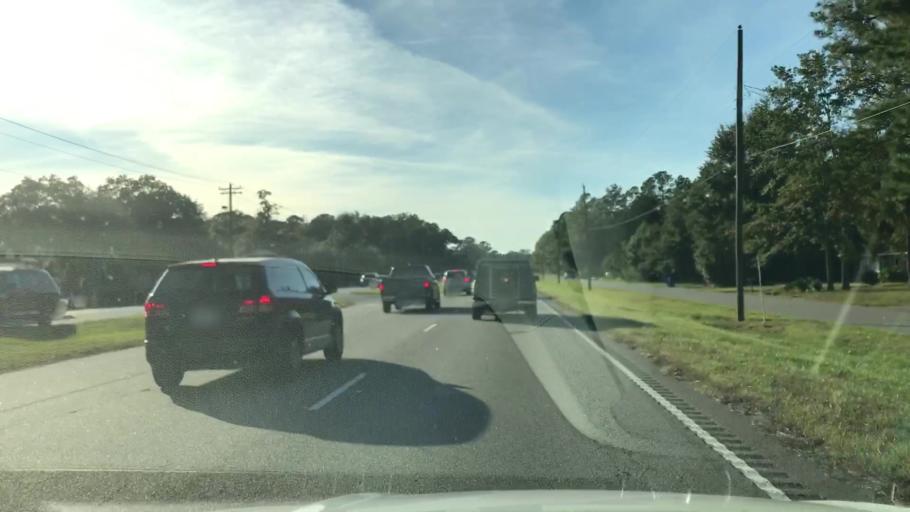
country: US
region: South Carolina
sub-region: Charleston County
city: Shell Point
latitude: 32.7961
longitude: -80.0755
